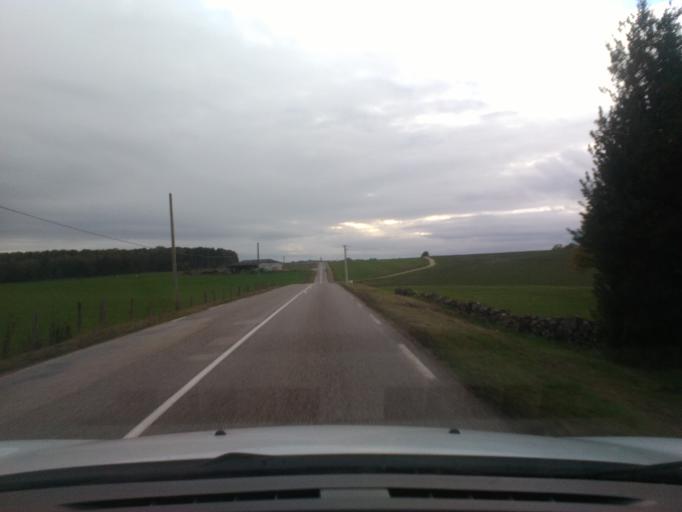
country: FR
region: Lorraine
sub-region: Departement des Vosges
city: Rambervillers
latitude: 48.3568
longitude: 6.5795
